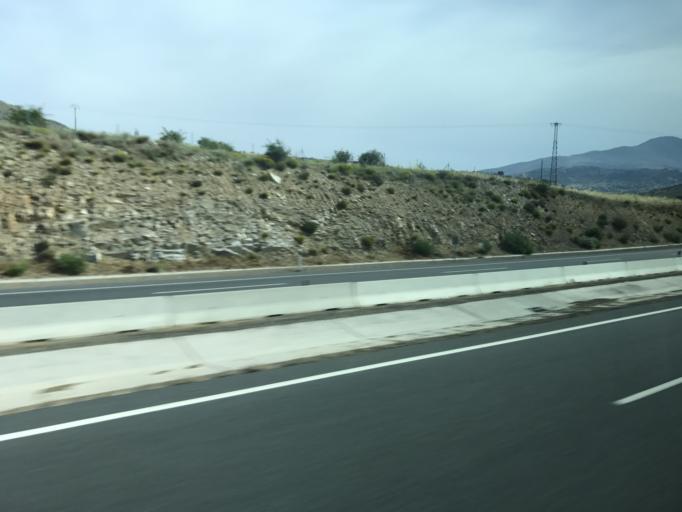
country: ES
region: Castille and Leon
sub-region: Provincia de Segovia
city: Vegas de Matute
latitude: 40.7373
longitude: -4.2659
